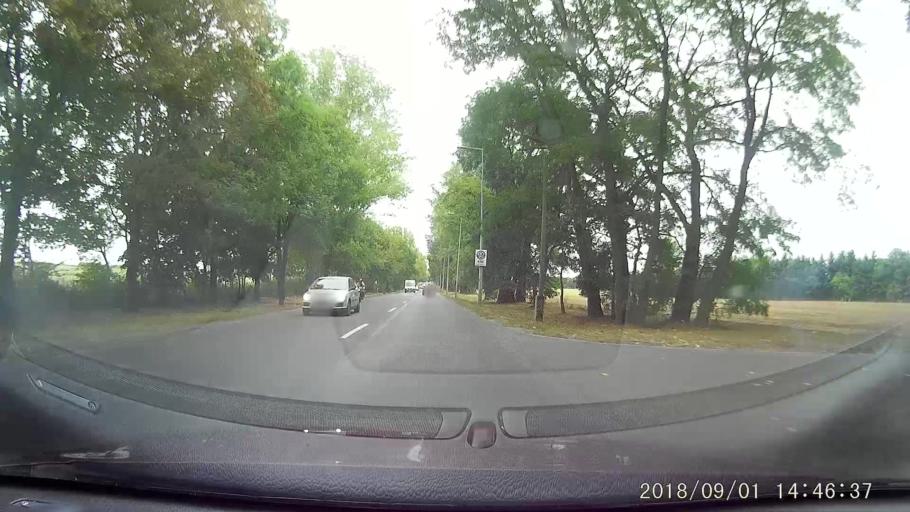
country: PL
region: Lubusz
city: Gorzow Wielkopolski
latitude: 52.7417
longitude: 15.1763
